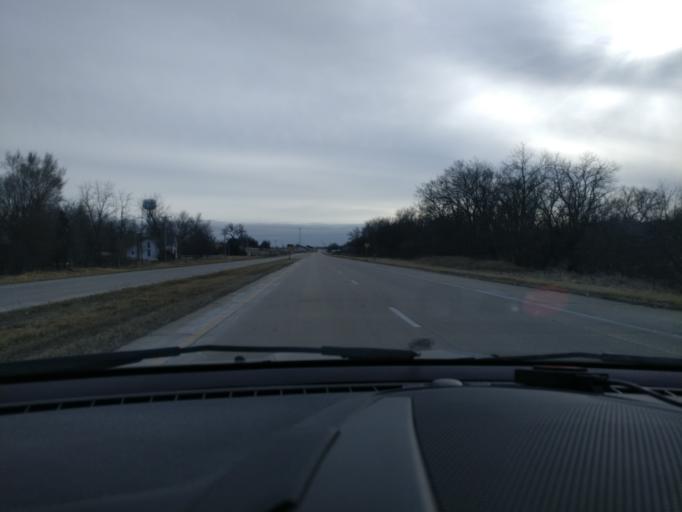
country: US
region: Nebraska
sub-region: Saunders County
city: Wahoo
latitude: 41.0654
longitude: -96.6404
